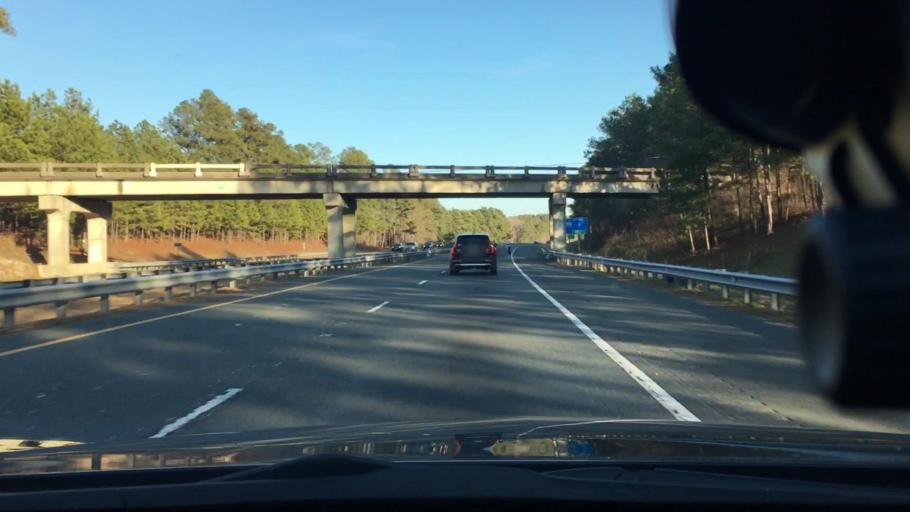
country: US
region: North Carolina
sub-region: Chatham County
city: Fearrington Village
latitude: 35.6445
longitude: -79.0144
